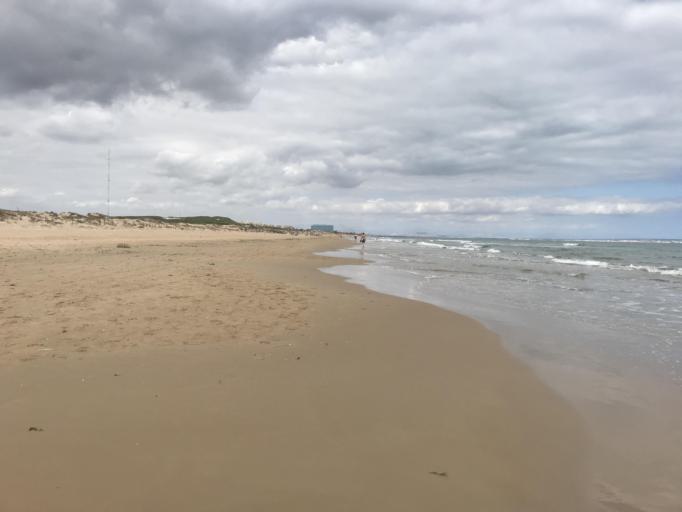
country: ES
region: Valencia
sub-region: Provincia de Alicante
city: Guardamar del Segura
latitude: 38.0439
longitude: -0.6514
